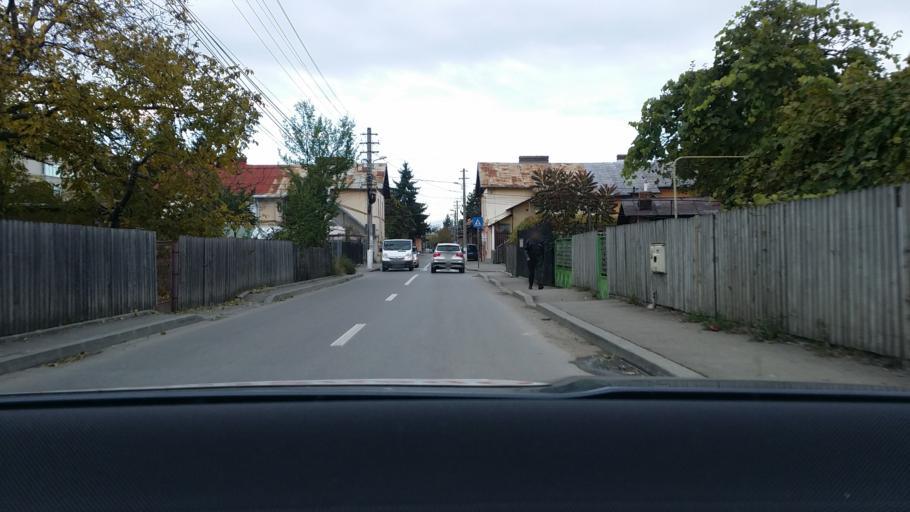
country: RO
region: Prahova
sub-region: Municipiul Campina
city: Campina
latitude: 45.1217
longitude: 25.7408
